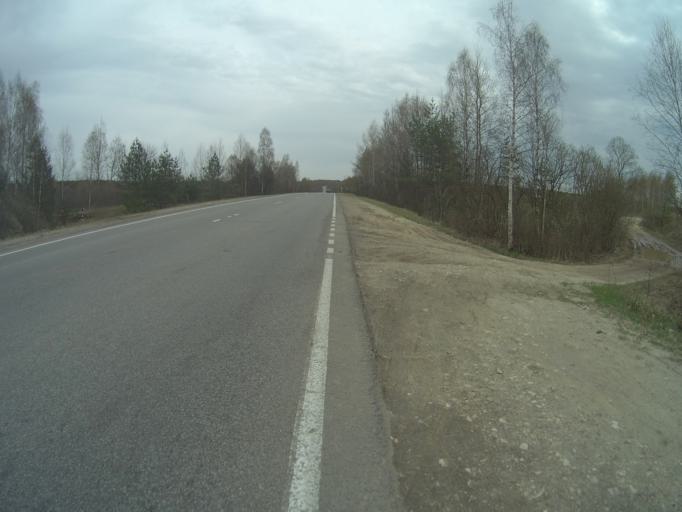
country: RU
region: Vladimir
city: Golovino
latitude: 55.9569
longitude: 40.5655
